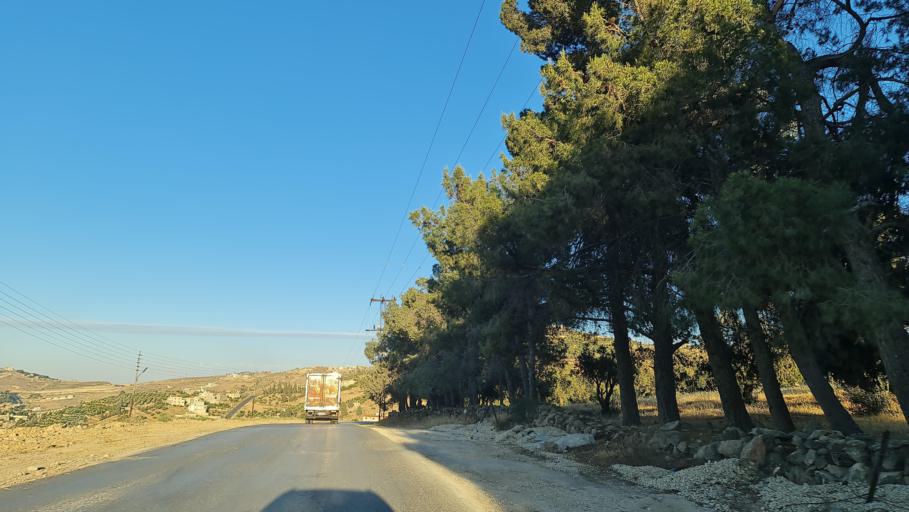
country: JO
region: Amman
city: Al Jubayhah
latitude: 32.0919
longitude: 35.9303
